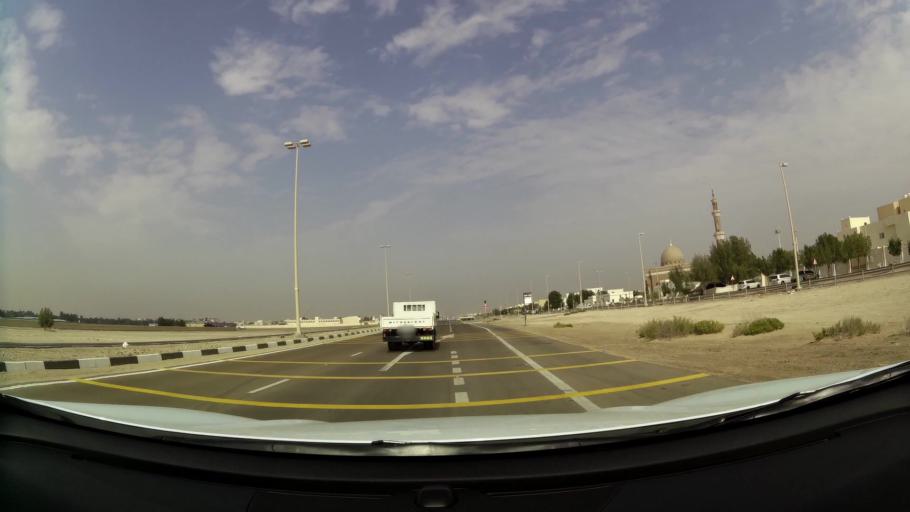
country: AE
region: Abu Dhabi
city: Abu Dhabi
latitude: 24.2826
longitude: 54.6584
